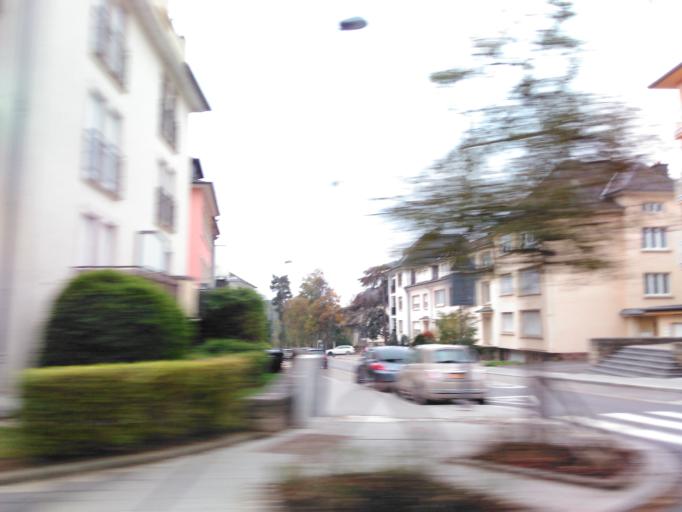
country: LU
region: Luxembourg
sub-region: Canton de Luxembourg
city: Luxembourg
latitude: 49.6195
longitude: 6.1163
